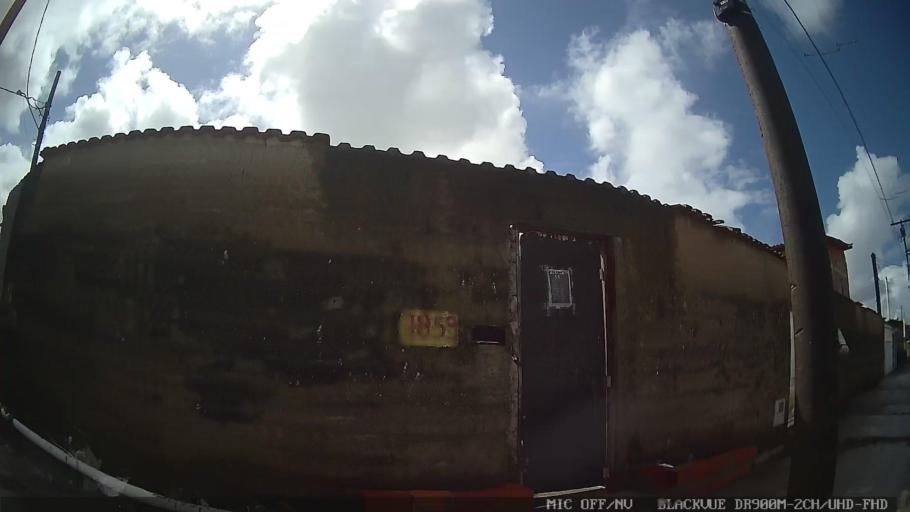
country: BR
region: Sao Paulo
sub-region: Itanhaem
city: Itanhaem
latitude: -24.2282
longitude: -46.8777
